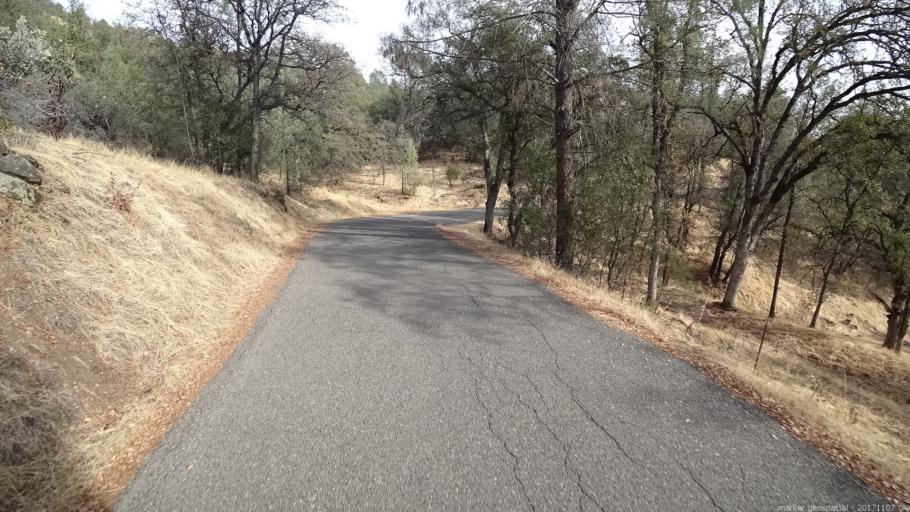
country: US
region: California
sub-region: Shasta County
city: Shasta
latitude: 40.5216
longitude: -122.5267
